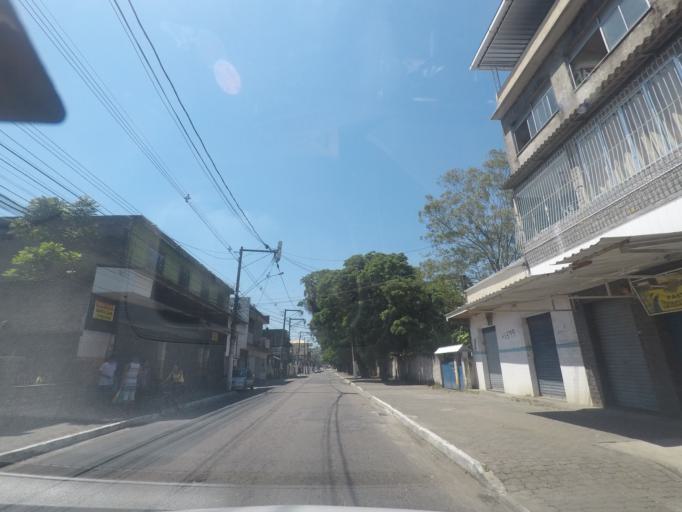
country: BR
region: Rio de Janeiro
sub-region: Petropolis
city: Petropolis
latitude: -22.5837
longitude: -43.1866
